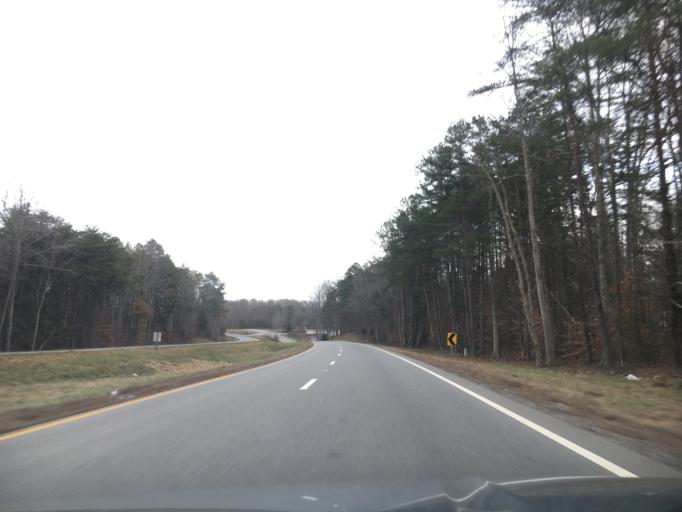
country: US
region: Virginia
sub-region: Prince Edward County
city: Hampden Sydney
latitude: 37.0898
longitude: -78.3856
